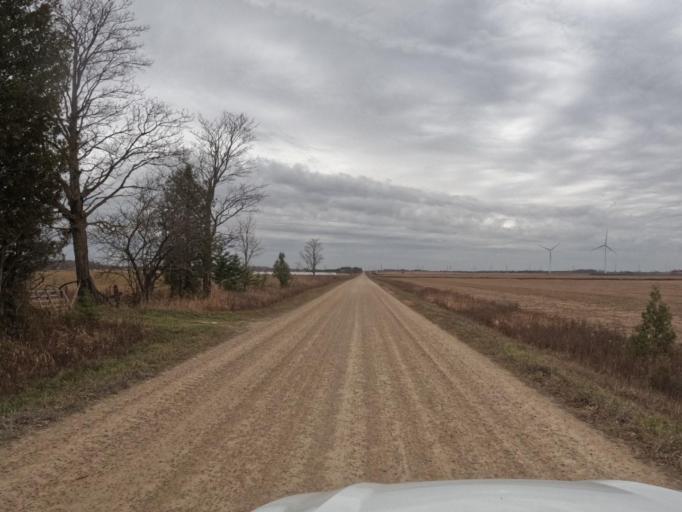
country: CA
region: Ontario
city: Shelburne
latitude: 44.0218
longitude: -80.3921
